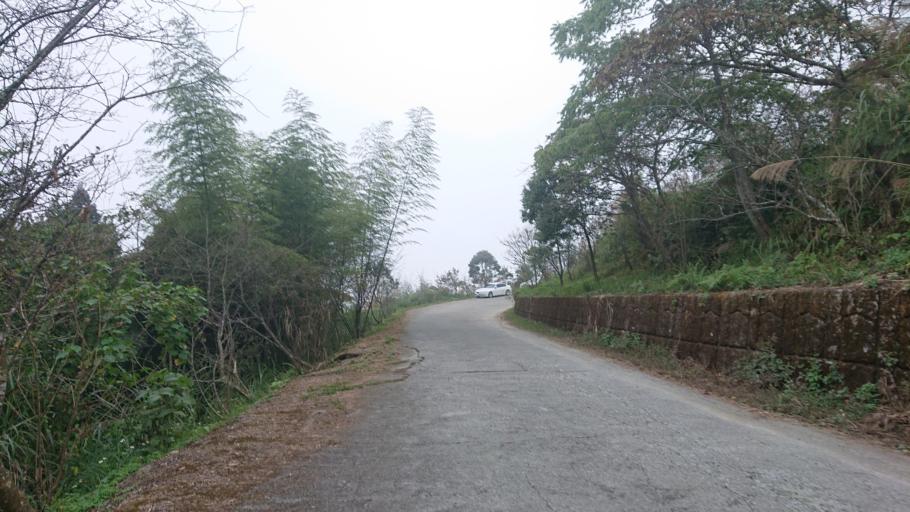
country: TW
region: Taiwan
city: Lugu
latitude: 23.6268
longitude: 120.7113
